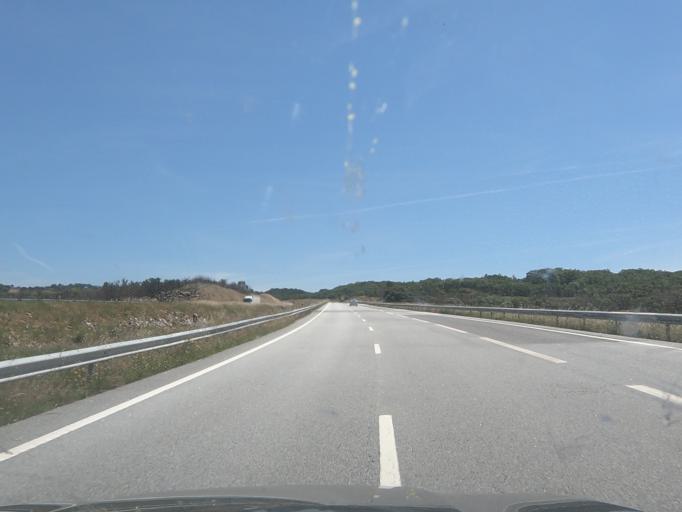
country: PT
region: Guarda
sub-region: Pinhel
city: Pinhel
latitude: 40.6041
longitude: -7.0264
